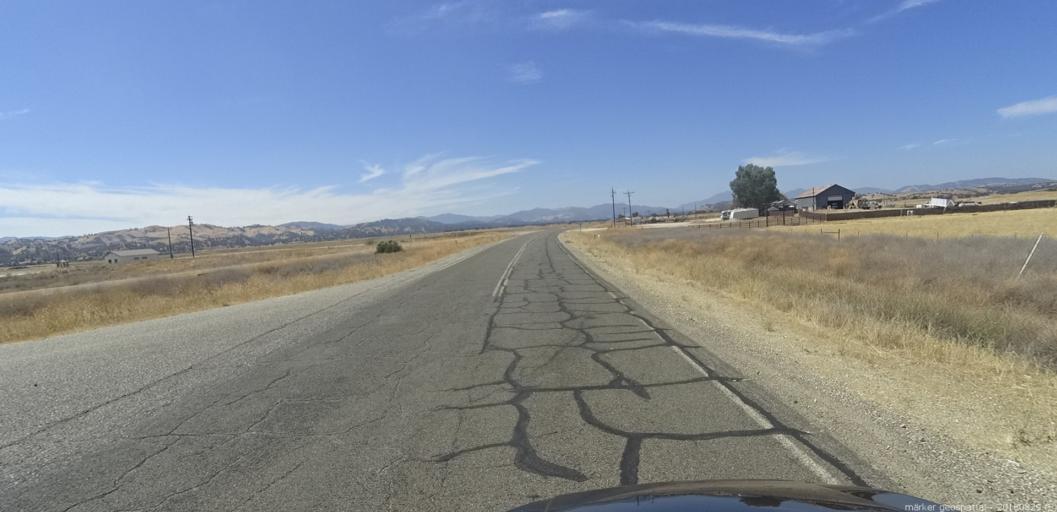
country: US
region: California
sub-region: Monterey County
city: King City
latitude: 35.9427
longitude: -121.1304
